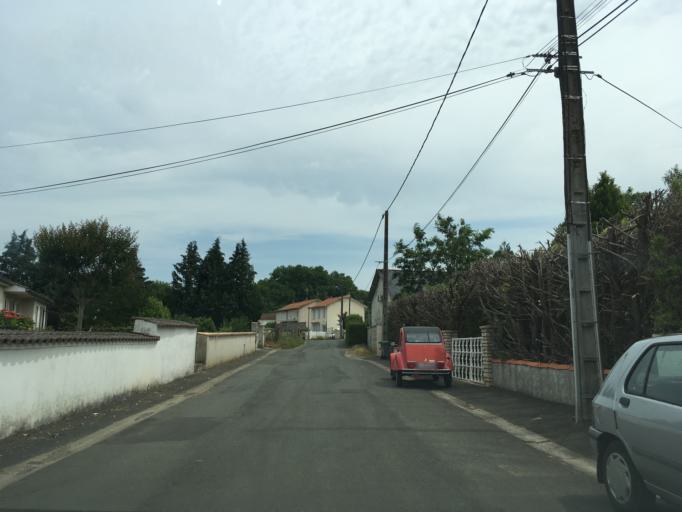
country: FR
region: Poitou-Charentes
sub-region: Departement des Deux-Sevres
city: Bessines
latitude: 46.3286
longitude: -0.5120
